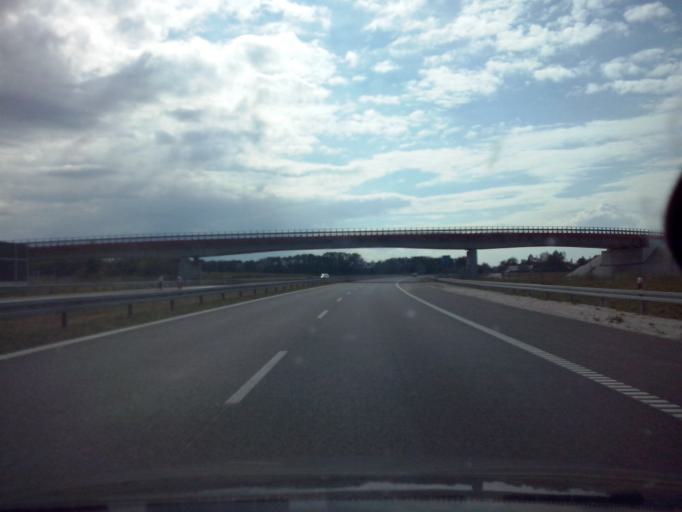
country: PL
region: Lesser Poland Voivodeship
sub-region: Powiat tarnowski
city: Lisia Gora
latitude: 50.0560
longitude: 21.0315
